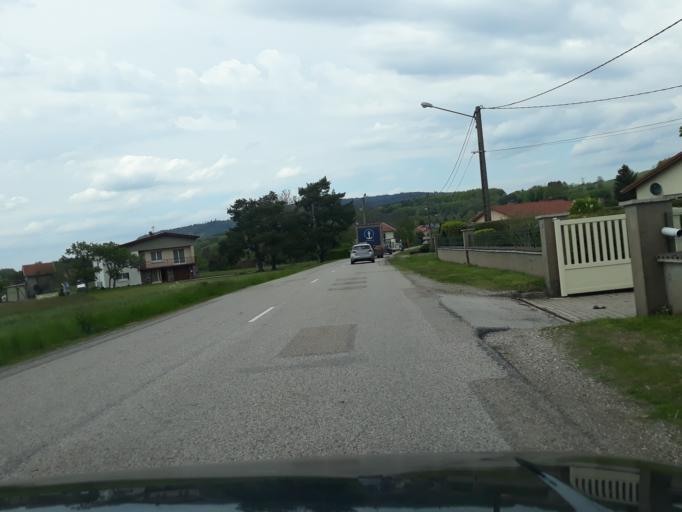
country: FR
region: Lorraine
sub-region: Departement des Vosges
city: Granges-sur-Vologne
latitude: 48.1629
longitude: 6.7772
